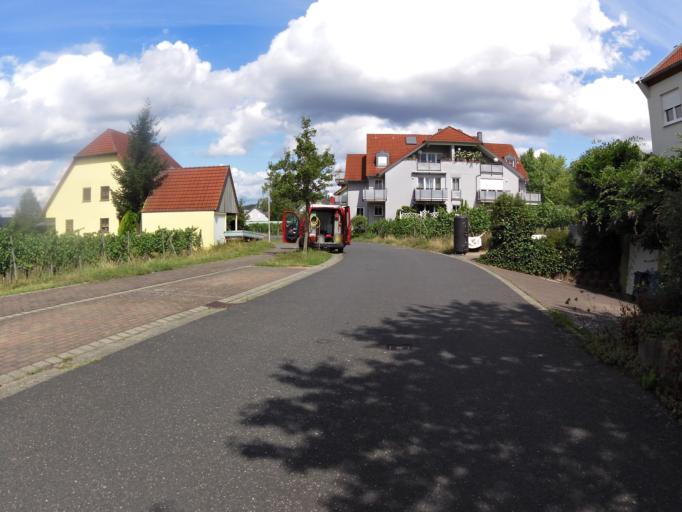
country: DE
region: Bavaria
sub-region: Regierungsbezirk Unterfranken
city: Sommerhausen
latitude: 49.6985
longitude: 10.0288
